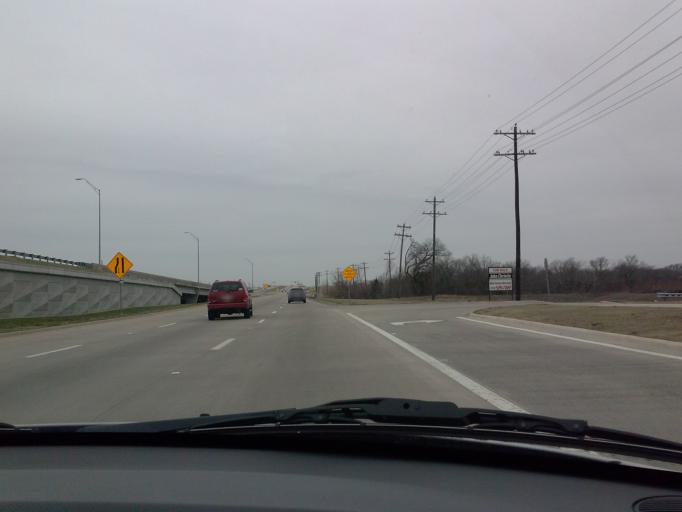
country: US
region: Texas
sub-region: Collin County
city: Frisco
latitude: 33.1193
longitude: -96.7515
